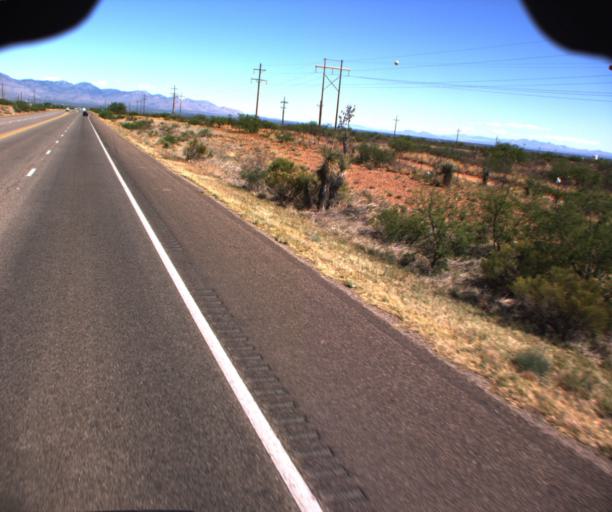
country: US
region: Arizona
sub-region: Cochise County
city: Huachuca City
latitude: 31.5902
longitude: -110.3226
